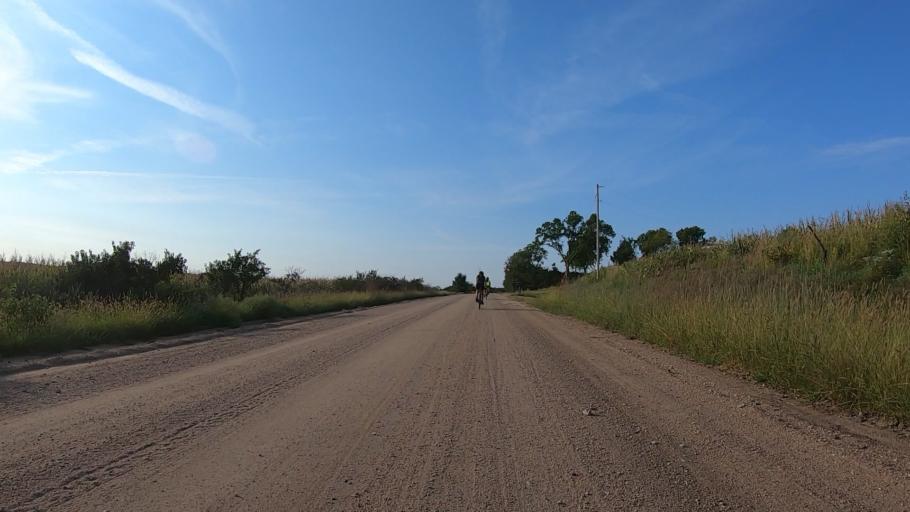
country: US
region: Kansas
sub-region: Marshall County
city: Blue Rapids
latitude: 39.6881
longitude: -96.7791
